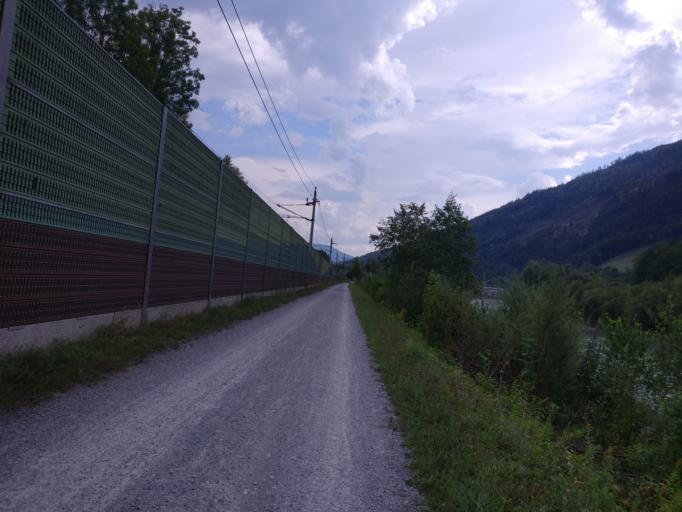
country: AT
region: Salzburg
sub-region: Politischer Bezirk Sankt Johann im Pongau
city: Pfarrwerfen
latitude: 47.4475
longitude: 13.2134
